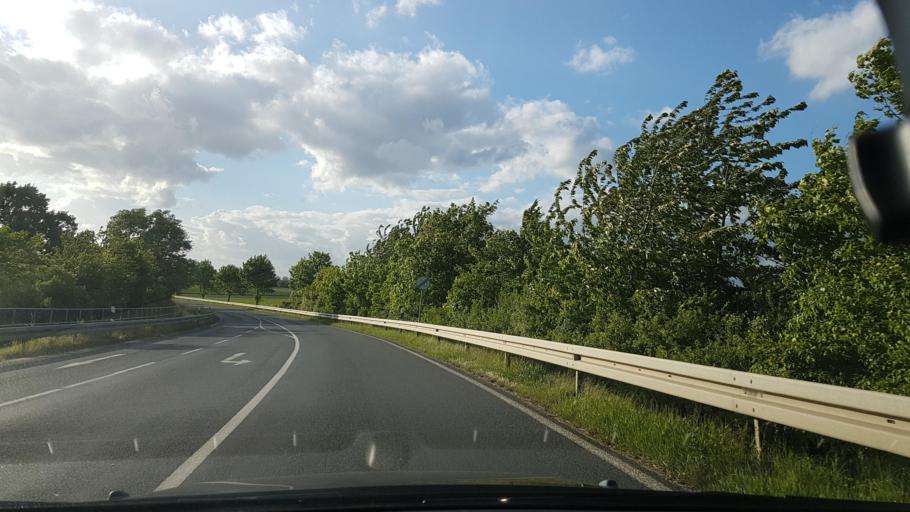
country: DE
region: Lower Saxony
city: Ronnenberg
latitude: 52.3056
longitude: 9.6341
